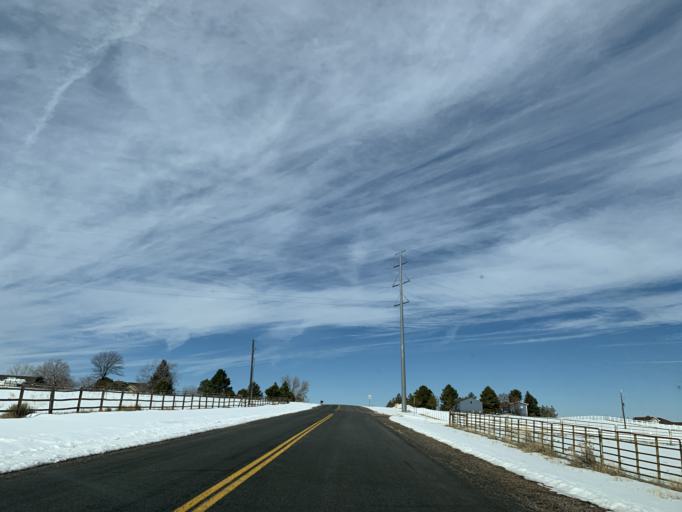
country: US
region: Colorado
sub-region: Douglas County
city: Carriage Club
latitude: 39.5156
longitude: -104.9035
